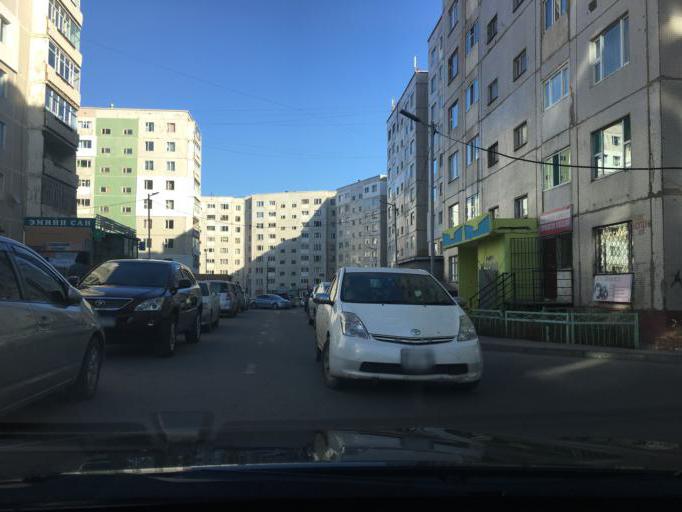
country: MN
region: Ulaanbaatar
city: Ulaanbaatar
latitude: 47.9256
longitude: 106.8800
